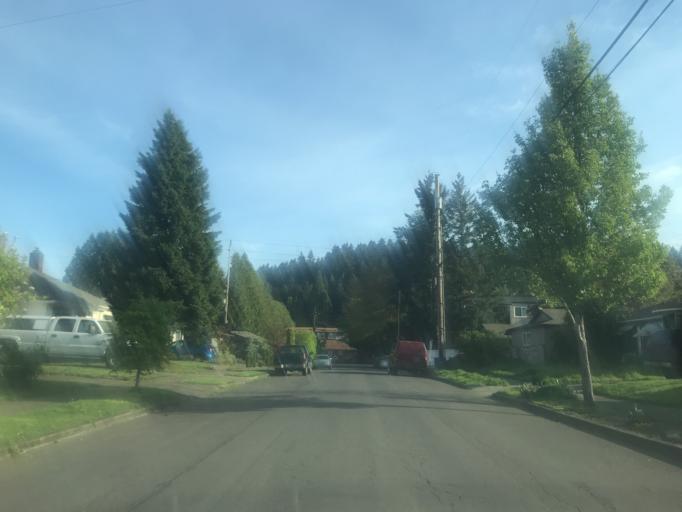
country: US
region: Oregon
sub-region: Multnomah County
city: Lents
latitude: 45.5043
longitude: -122.5956
